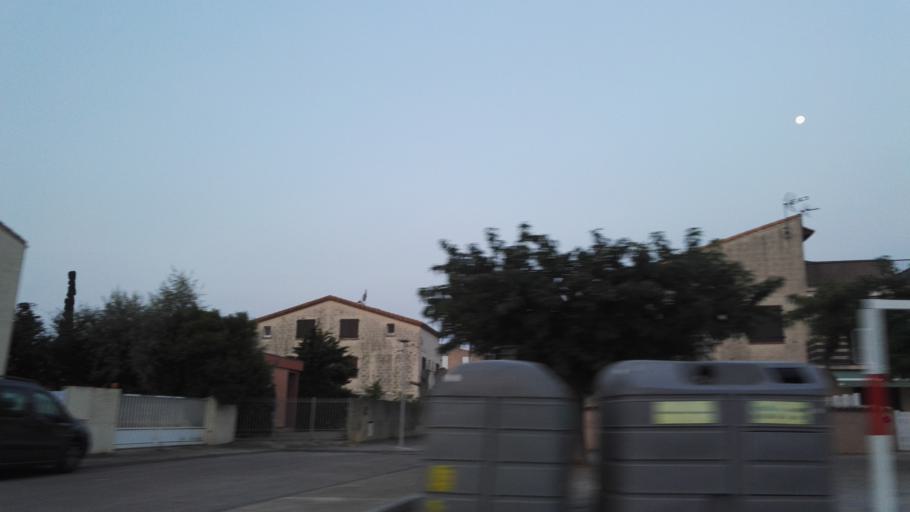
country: FR
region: Languedoc-Roussillon
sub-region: Departement de l'Herault
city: Marseillan
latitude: 43.3193
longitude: 3.5541
